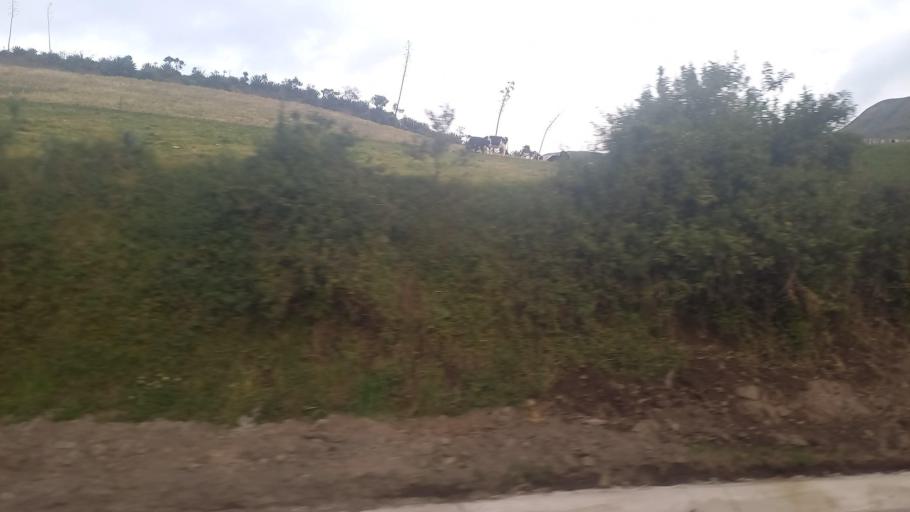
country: EC
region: Pichincha
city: Cayambe
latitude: 0.1308
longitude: -78.0686
